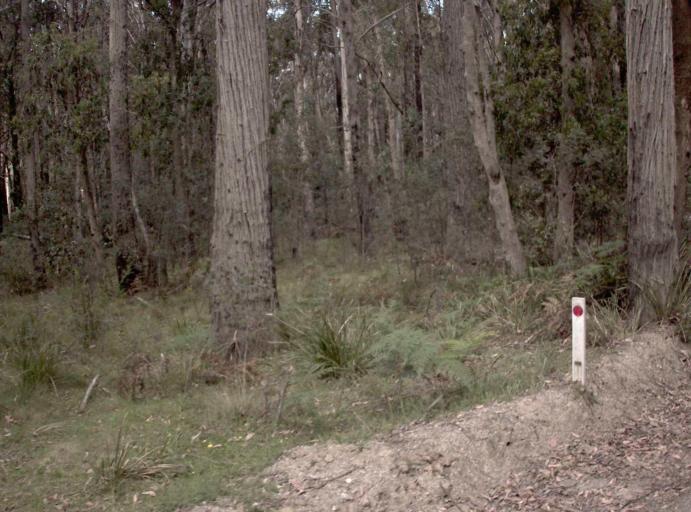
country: AU
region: New South Wales
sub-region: Bombala
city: Bombala
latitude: -37.1846
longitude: 148.7025
